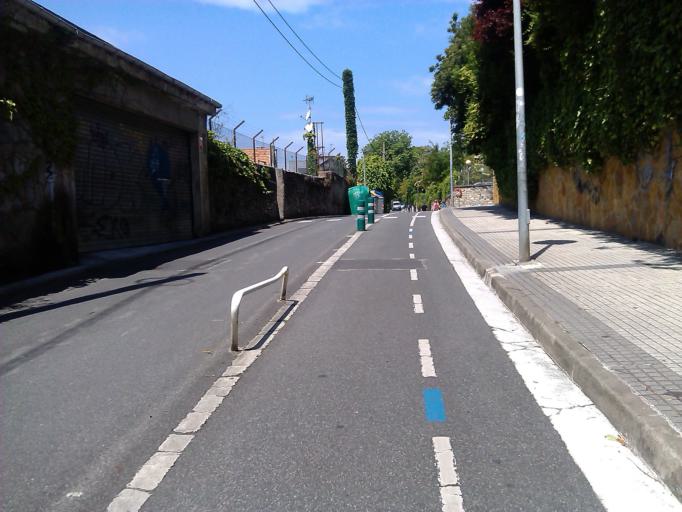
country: ES
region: Basque Country
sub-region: Provincia de Guipuzcoa
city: San Sebastian
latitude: 43.3226
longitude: -1.9629
